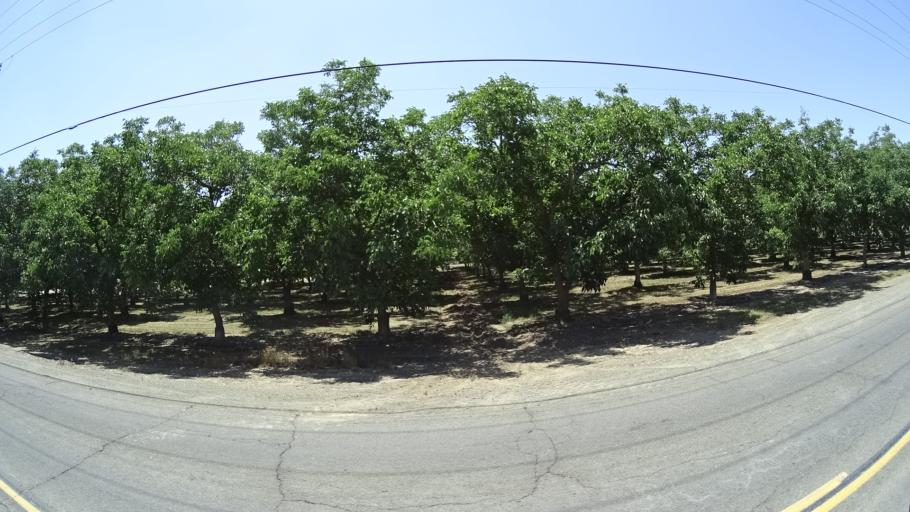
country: US
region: California
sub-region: Kings County
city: Lucerne
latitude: 36.3571
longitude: -119.6900
